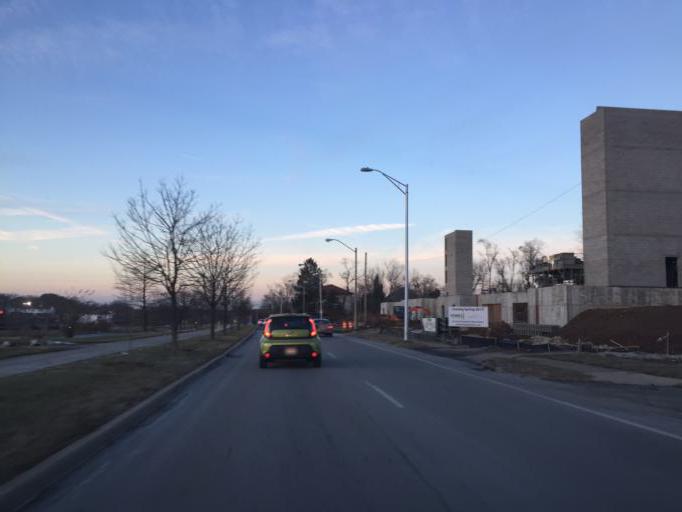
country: US
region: Indiana
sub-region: Monroe County
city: Bloomington
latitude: 39.1792
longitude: -86.5335
